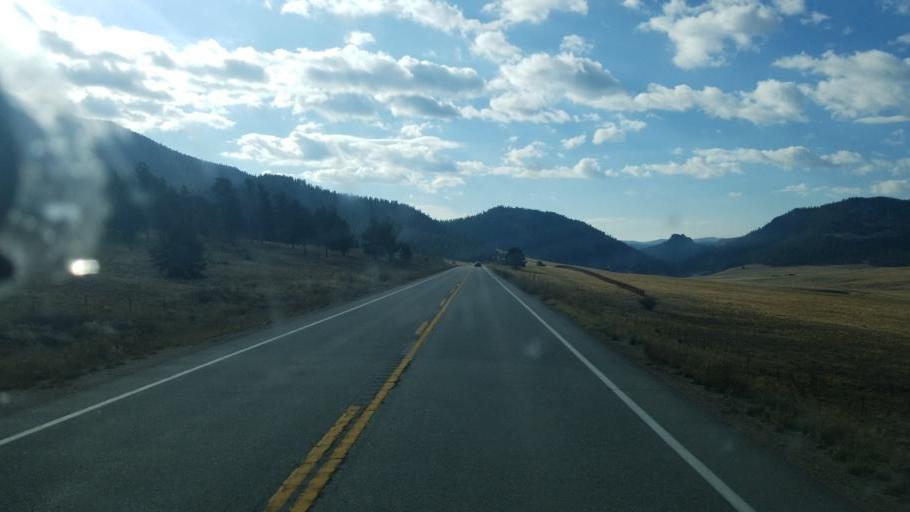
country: US
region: Colorado
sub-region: Chaffee County
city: Buena Vista
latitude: 38.8829
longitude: -105.9894
